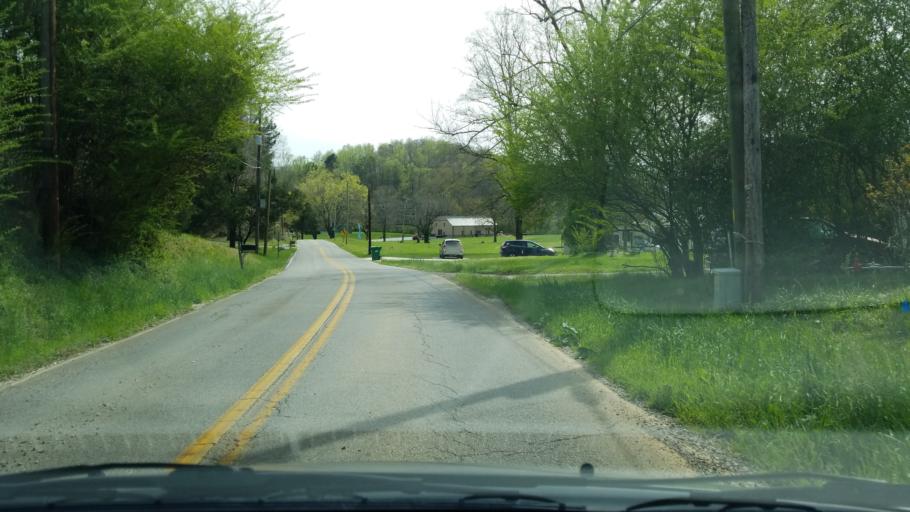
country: US
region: Tennessee
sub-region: Hamilton County
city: Falling Water
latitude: 35.1752
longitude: -85.2590
